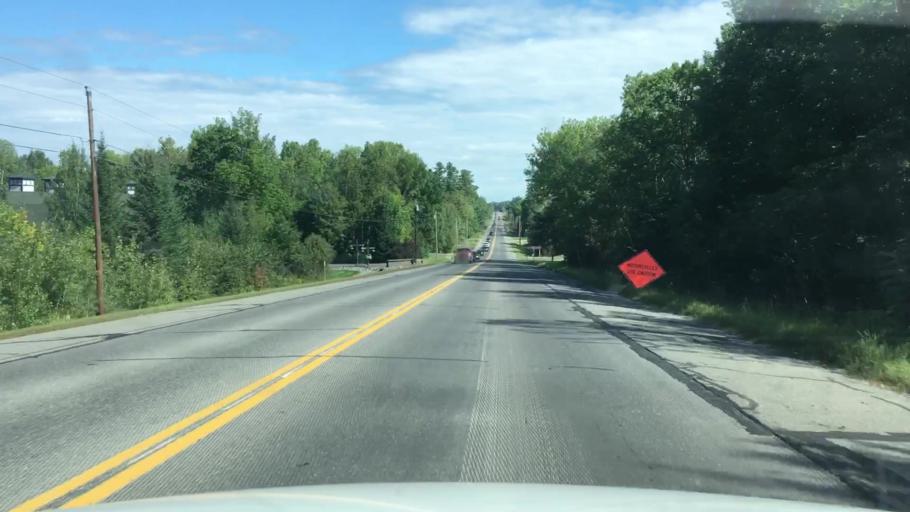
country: US
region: Maine
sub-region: Penobscot County
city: Corinna
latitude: 44.8831
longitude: -69.2789
